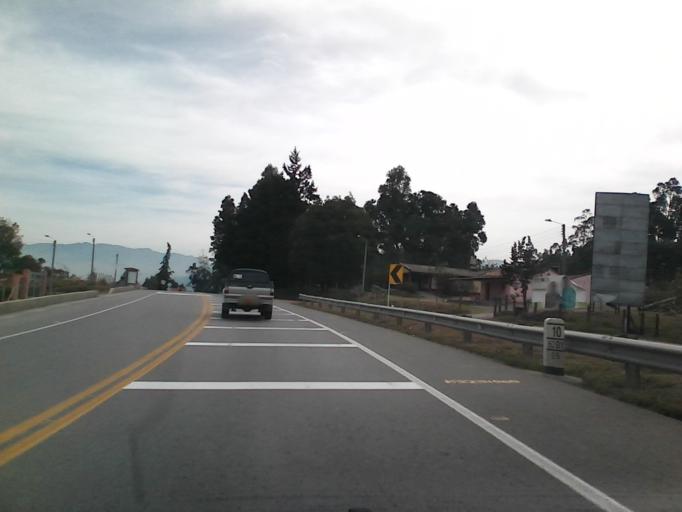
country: CO
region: Boyaca
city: Sogamoso
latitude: 5.7324
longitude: -72.9620
